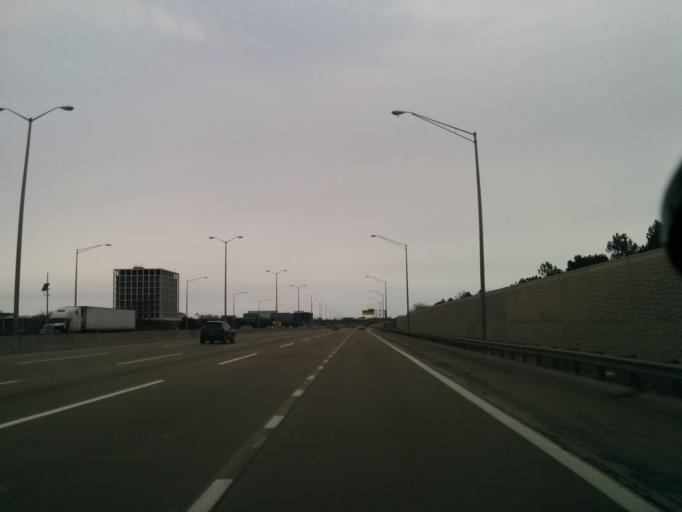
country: US
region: Illinois
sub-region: Cook County
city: Northbrook
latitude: 42.0971
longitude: -87.8679
